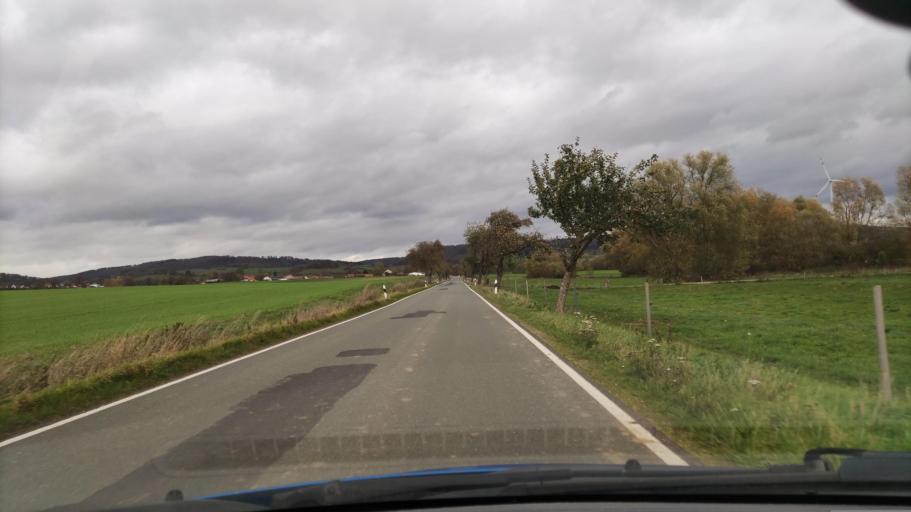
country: DE
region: Lower Saxony
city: Dassel
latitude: 51.8335
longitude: 9.7267
